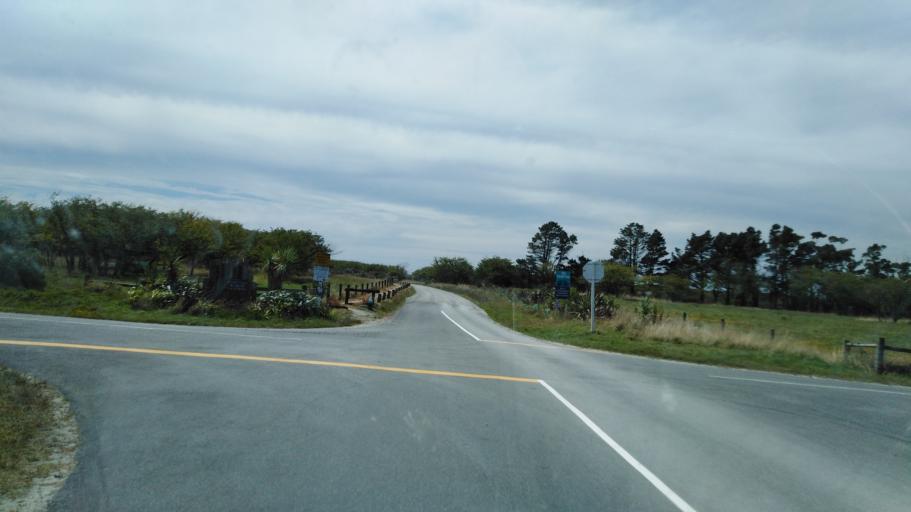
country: NZ
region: West Coast
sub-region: Buller District
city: Westport
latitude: -41.7387
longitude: 171.6040
